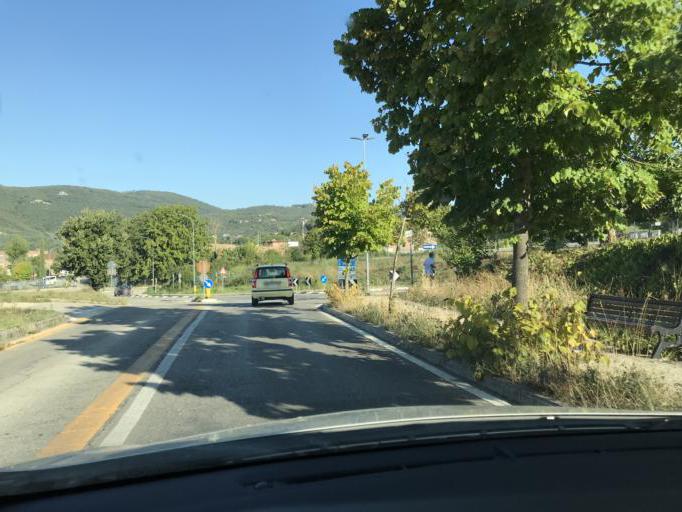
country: IT
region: Umbria
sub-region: Provincia di Perugia
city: Perugia
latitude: 43.1178
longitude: 12.3591
